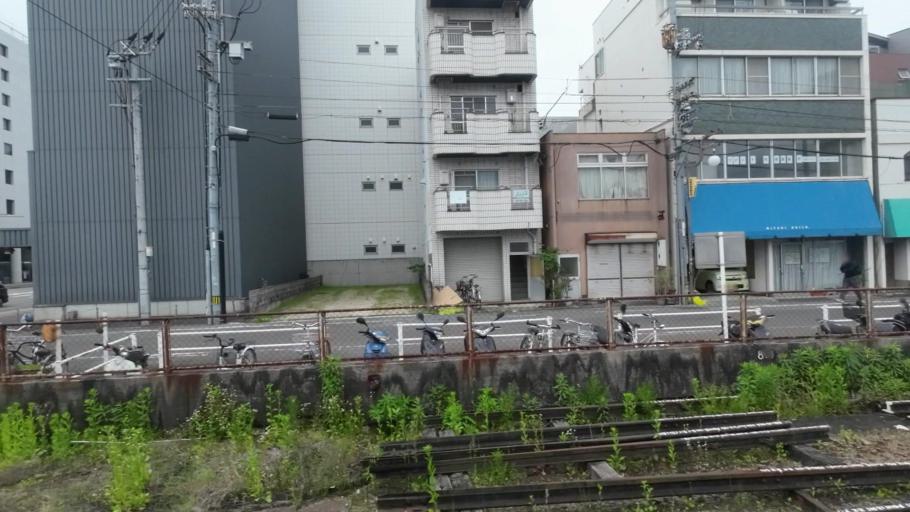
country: JP
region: Tokushima
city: Tokushima-shi
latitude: 34.0759
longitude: 134.5484
